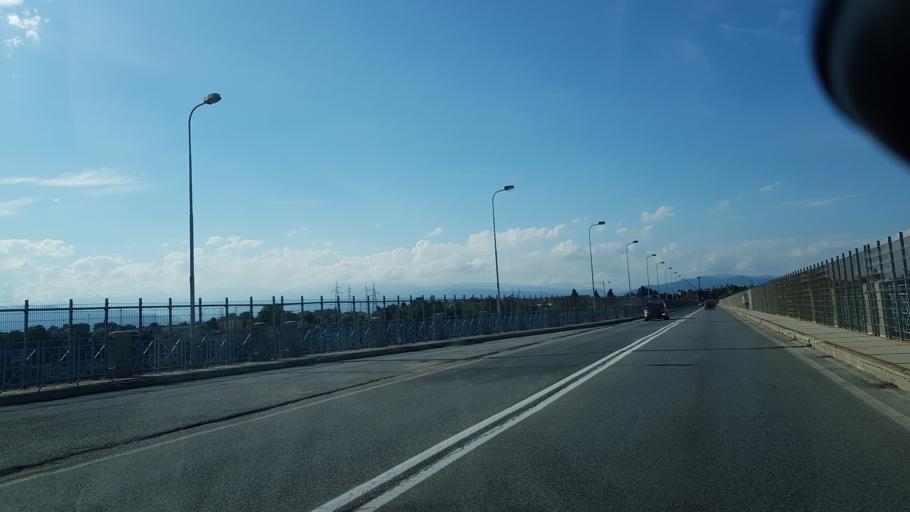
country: IT
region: Piedmont
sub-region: Provincia di Cuneo
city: Cuneo
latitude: 44.3937
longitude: 7.5412
